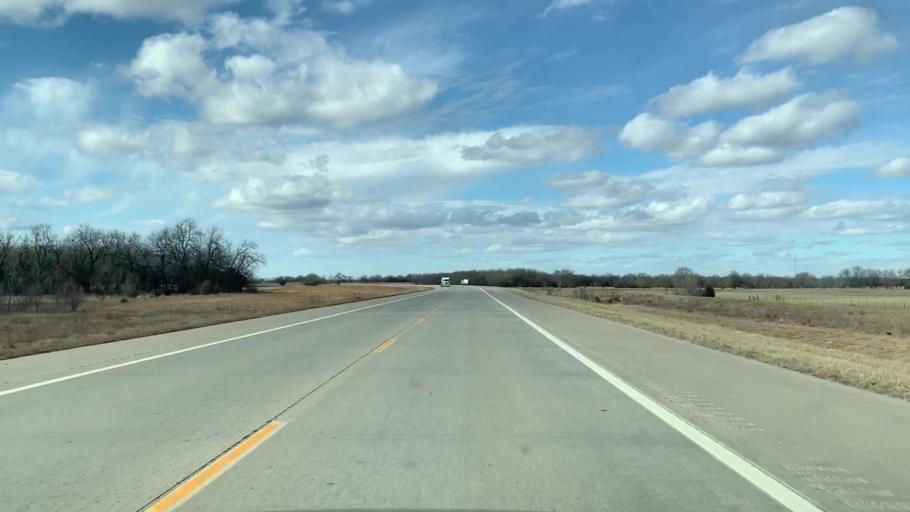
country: US
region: Kansas
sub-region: Labette County
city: Parsons
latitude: 37.3563
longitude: -95.2154
